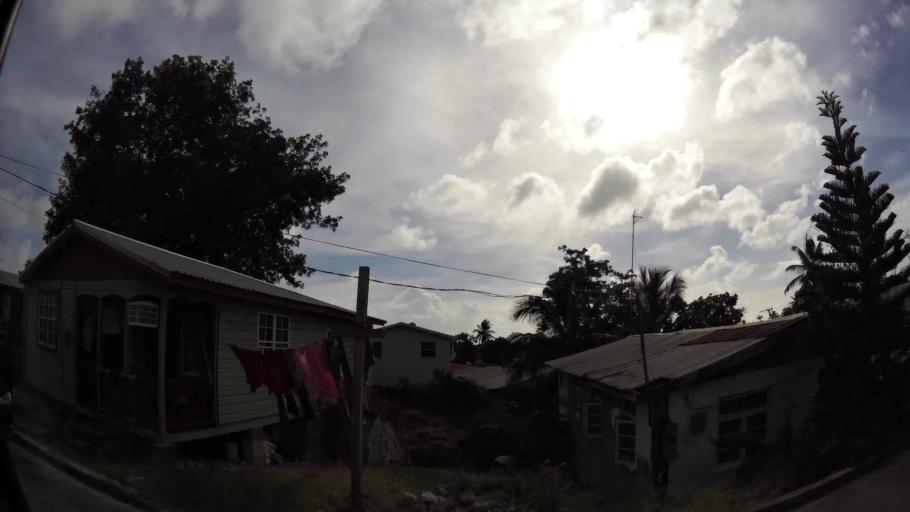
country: BB
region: Saint Michael
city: Bridgetown
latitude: 13.0878
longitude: -59.5902
